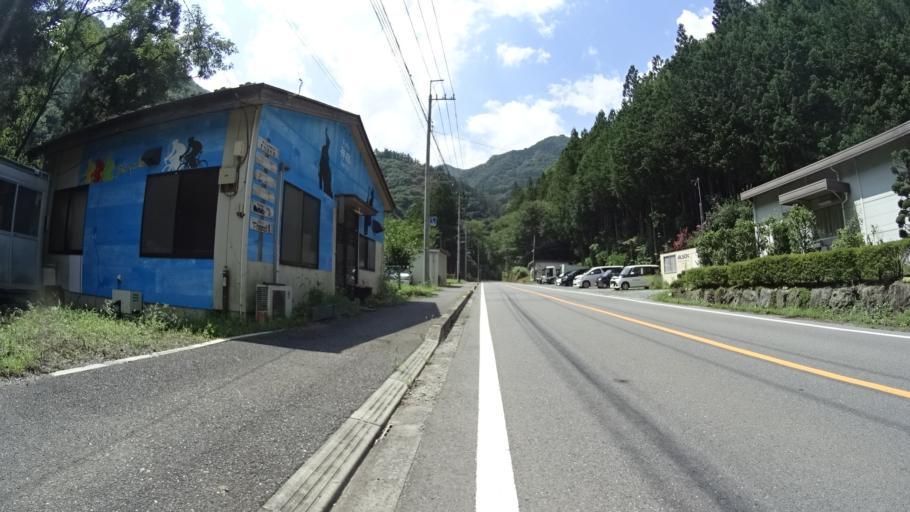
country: JP
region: Gunma
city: Tomioka
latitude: 36.0787
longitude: 138.7833
